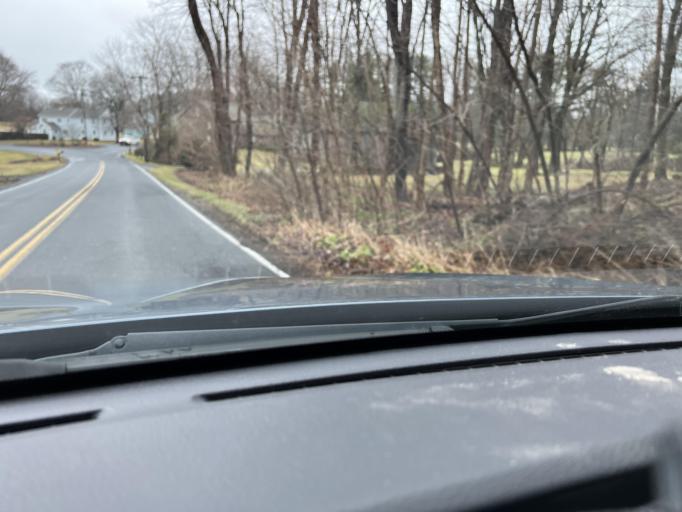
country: US
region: Massachusetts
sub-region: Hampden County
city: Southwick
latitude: 42.0368
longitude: -72.7132
